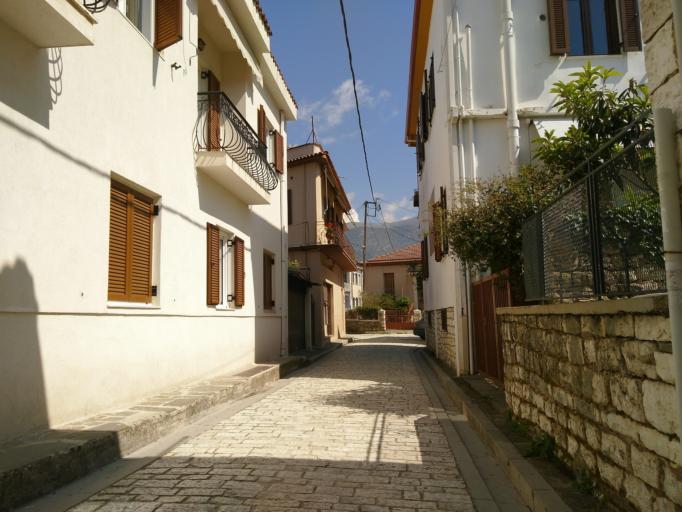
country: GR
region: Epirus
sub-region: Nomos Ioanninon
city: Ioannina
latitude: 39.6713
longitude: 20.8600
